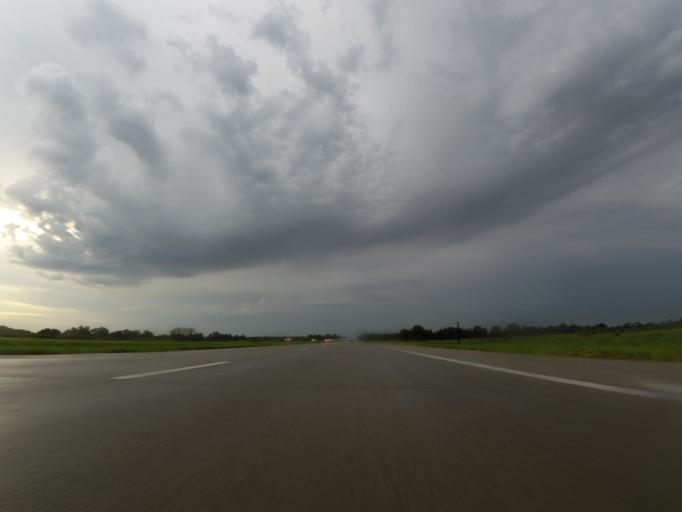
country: US
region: Kansas
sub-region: Reno County
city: Haven
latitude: 37.9249
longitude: -97.8397
